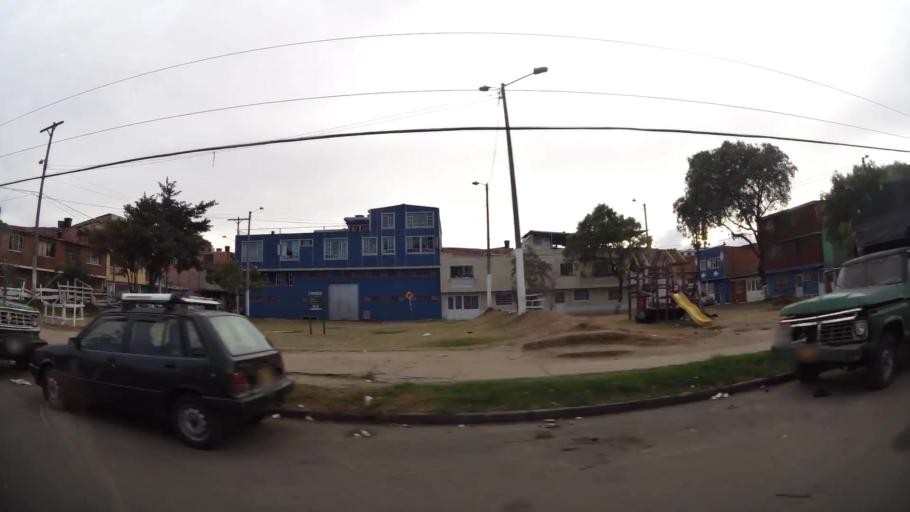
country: CO
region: Cundinamarca
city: Soacha
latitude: 4.6241
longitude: -74.1603
